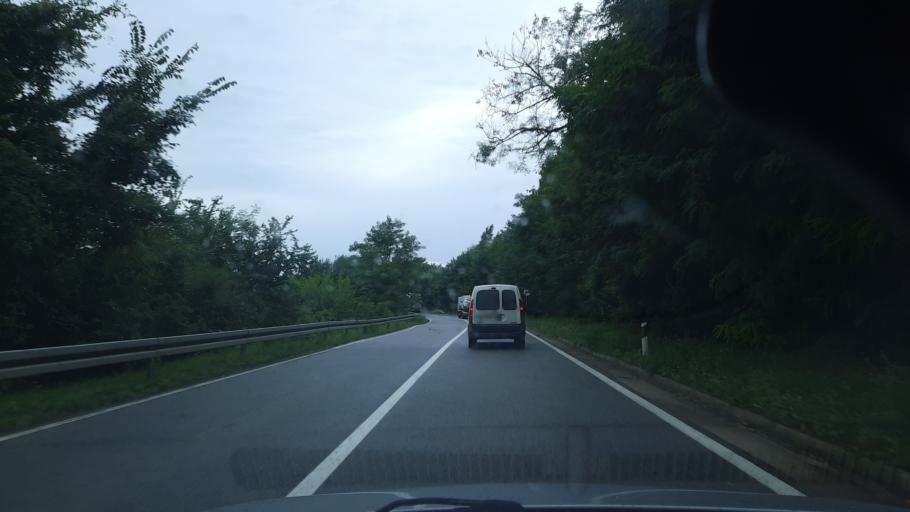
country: RS
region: Central Serbia
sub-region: Raski Okrug
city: Kraljevo
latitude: 43.7639
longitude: 20.8061
